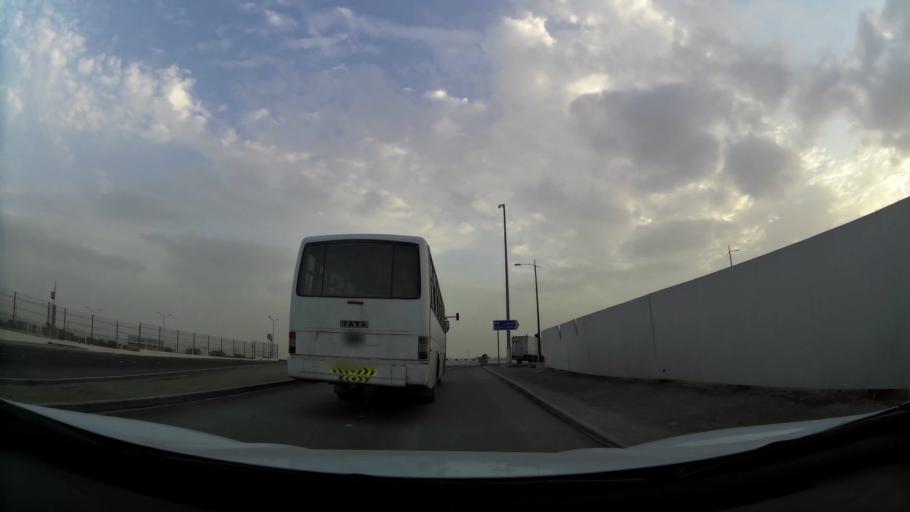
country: AE
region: Abu Dhabi
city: Abu Dhabi
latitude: 24.5321
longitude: 54.4188
